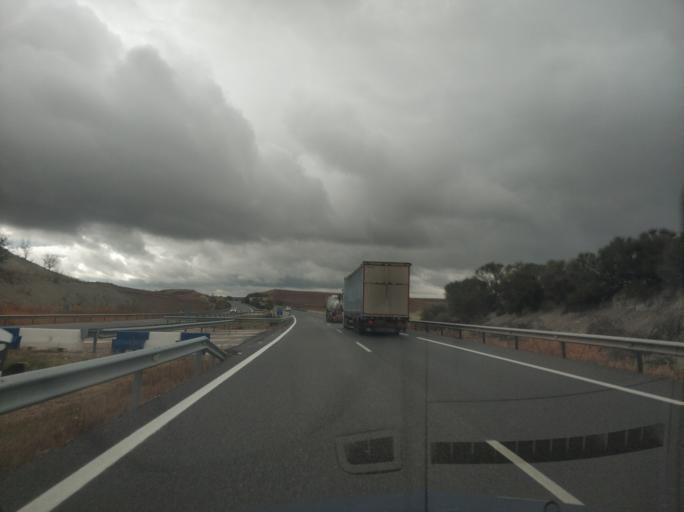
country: ES
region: Castille and Leon
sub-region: Provincia de Palencia
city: Soto de Cerrato
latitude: 41.9667
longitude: -4.4565
